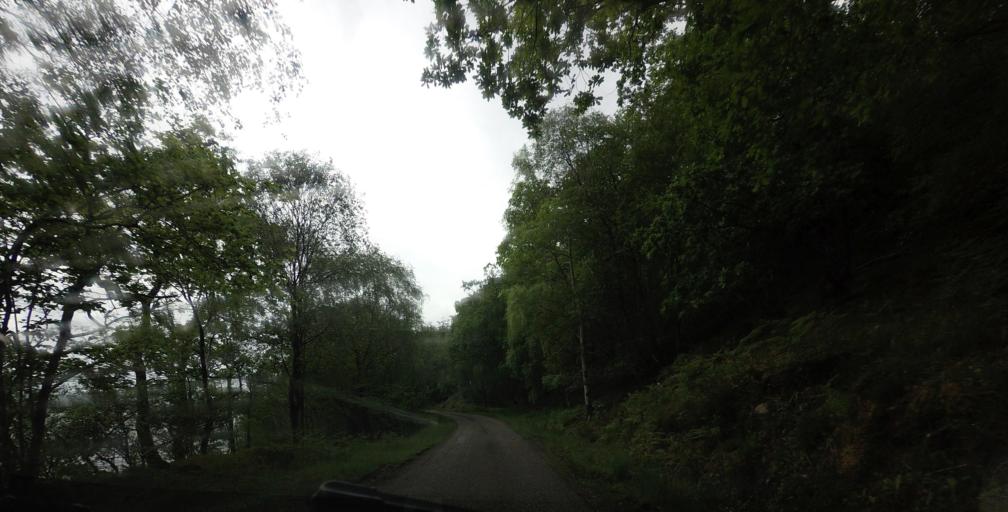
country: GB
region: Scotland
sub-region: Highland
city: Fort William
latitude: 56.7843
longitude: -5.1889
